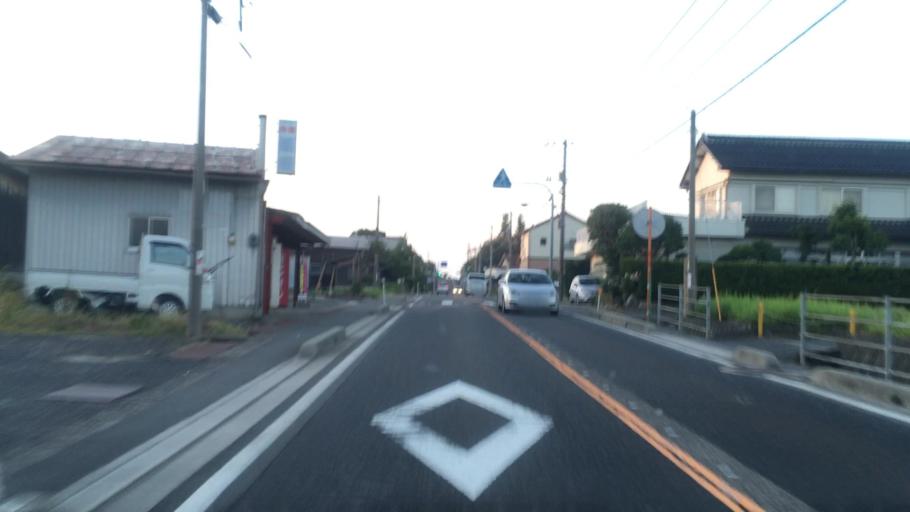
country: JP
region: Tottori
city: Tottori
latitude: 35.5846
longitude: 134.3326
